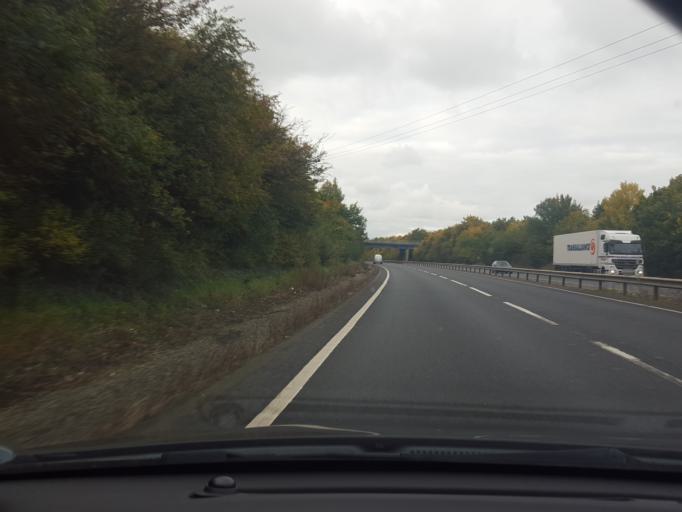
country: GB
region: England
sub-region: Suffolk
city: Stowmarket
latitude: 52.1932
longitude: 1.0133
